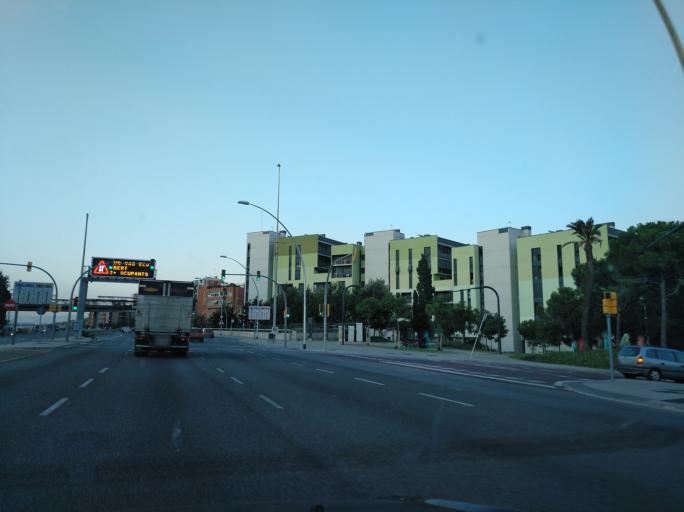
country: ES
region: Catalonia
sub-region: Provincia de Barcelona
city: Nou Barris
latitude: 41.4491
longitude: 2.1886
